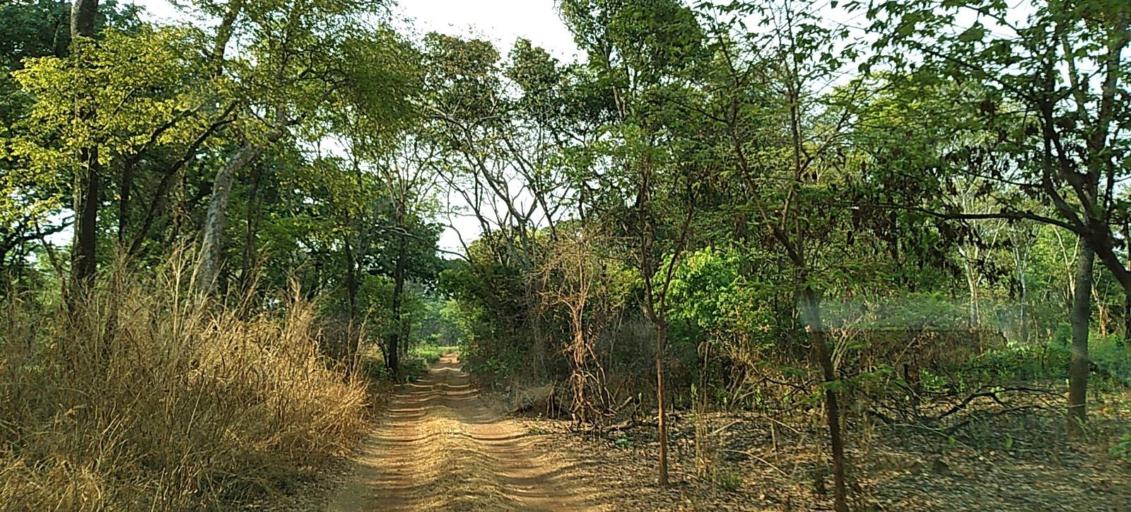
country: ZM
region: Copperbelt
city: Kalulushi
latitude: -12.9849
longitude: 27.7193
